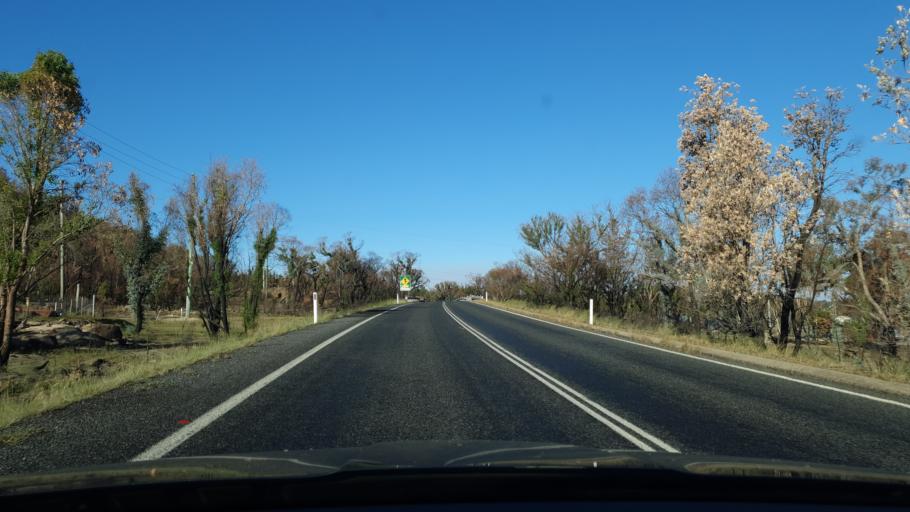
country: AU
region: Queensland
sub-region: Southern Downs
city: Stanthorpe
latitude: -28.6516
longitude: 151.9199
